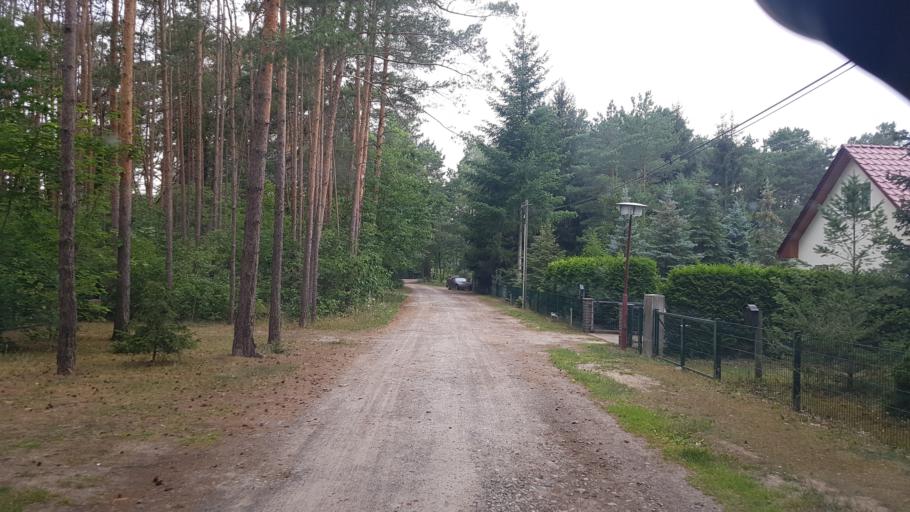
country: DE
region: Brandenburg
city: Gross Koris
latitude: 52.1609
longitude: 13.6952
